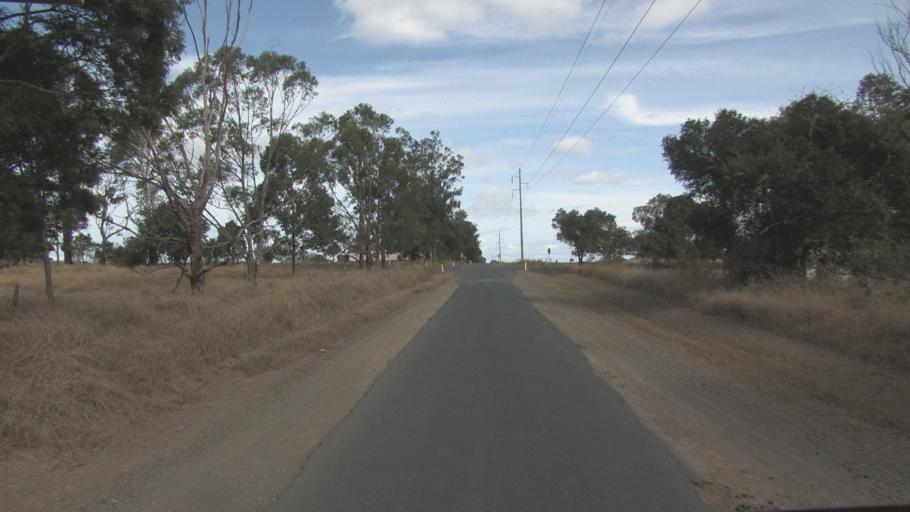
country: AU
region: Queensland
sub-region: Logan
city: Cedar Vale
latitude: -27.9198
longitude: 153.0129
